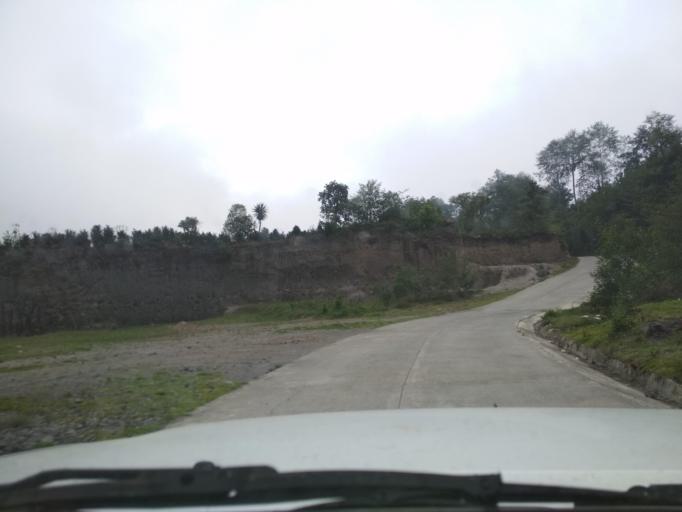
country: MX
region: Veracruz
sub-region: La Perla
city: Metlac Hernandez (Metlac Primero)
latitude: 18.9552
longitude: -97.1739
